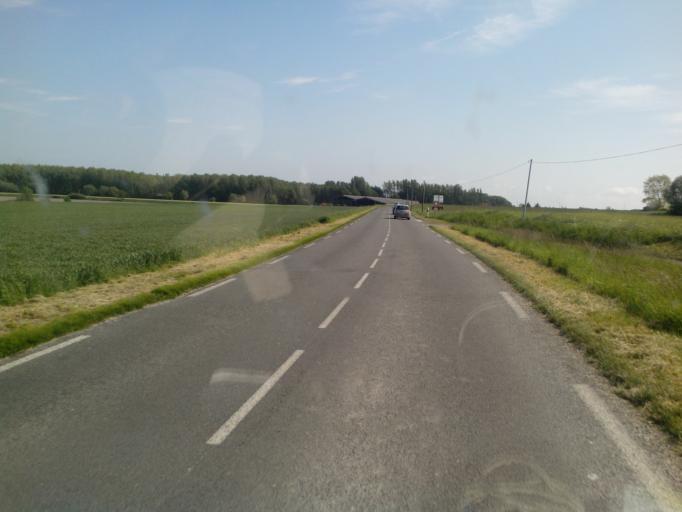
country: FR
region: Picardie
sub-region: Departement de la Somme
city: Quend
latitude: 50.3350
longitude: 1.6437
